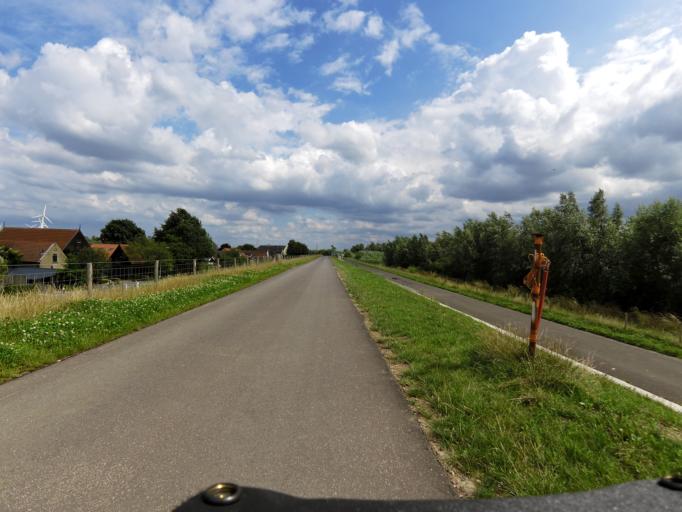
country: NL
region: South Holland
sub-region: Gemeente Strijen
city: Strijen
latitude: 51.7146
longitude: 4.5822
